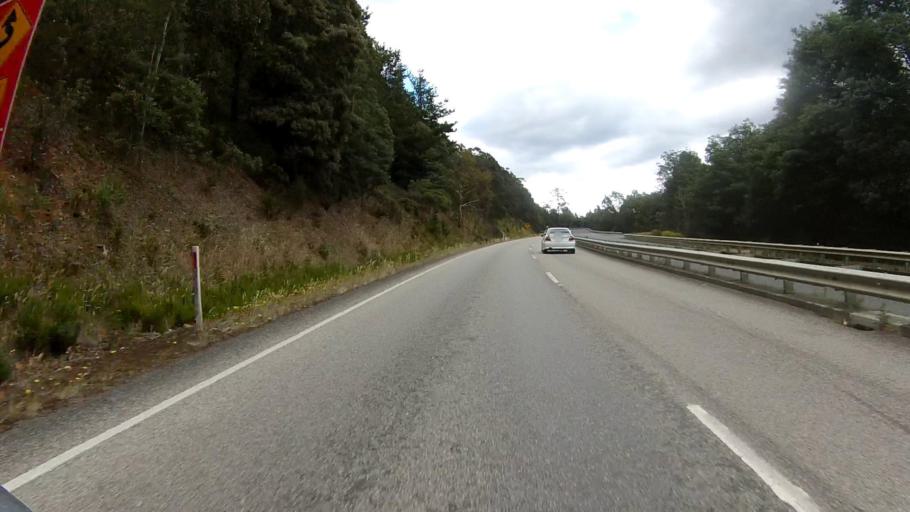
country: AU
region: Tasmania
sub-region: Kingborough
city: Margate
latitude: -42.9842
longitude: 147.1795
